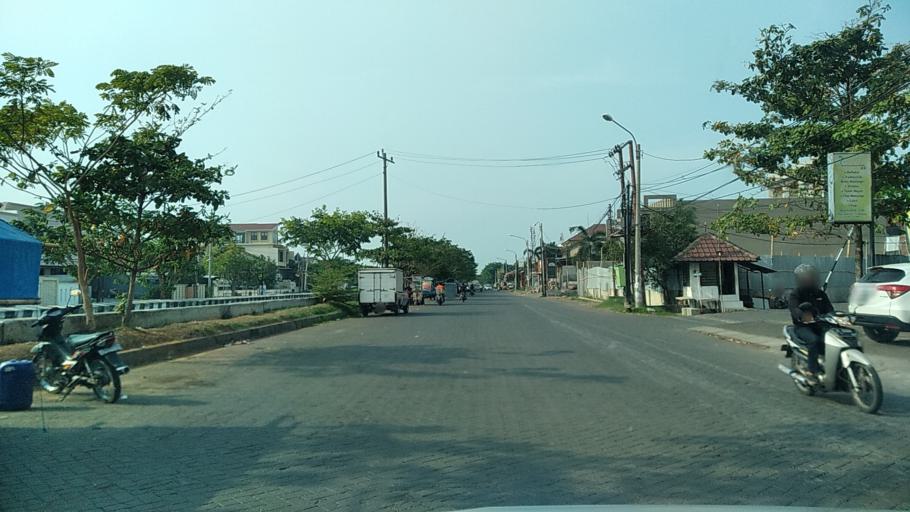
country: ID
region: Central Java
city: Semarang
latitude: -6.9626
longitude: 110.4108
